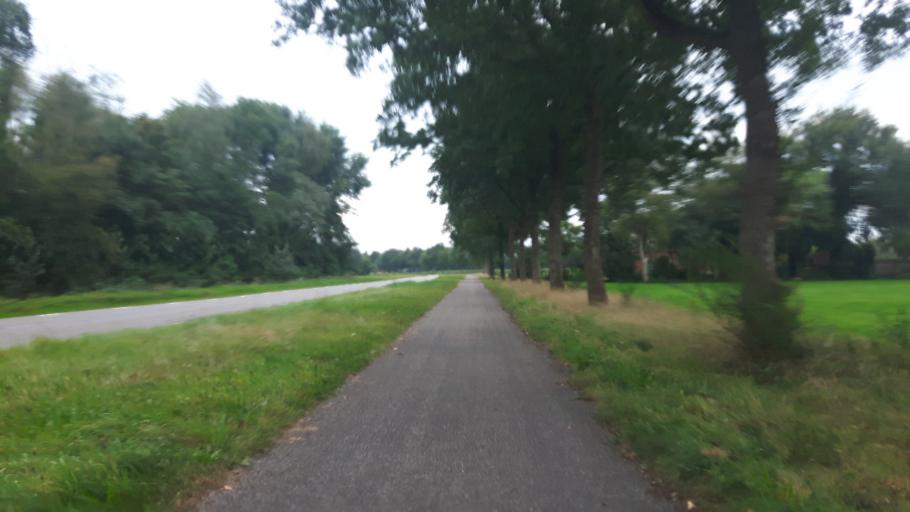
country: NL
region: Friesland
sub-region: Gemeente Weststellingwerf
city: Noordwolde
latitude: 52.9621
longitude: 6.2206
